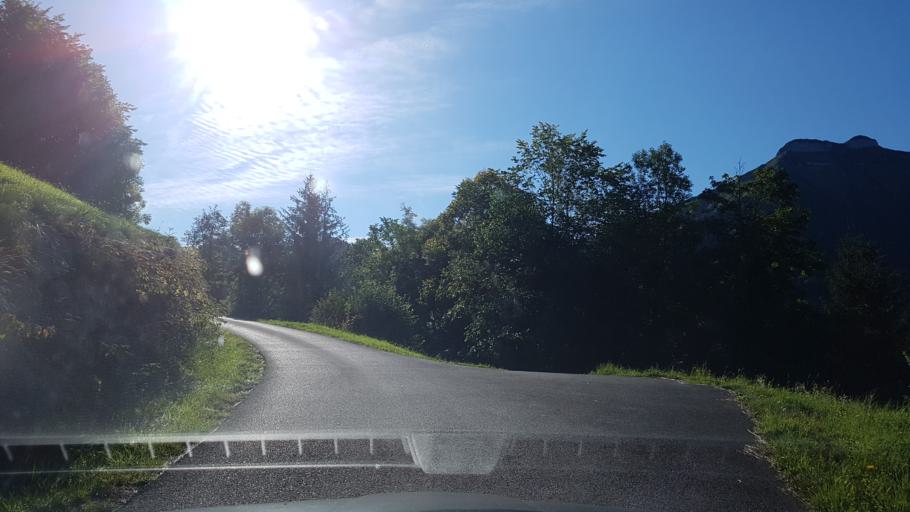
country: AT
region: Salzburg
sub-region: Politischer Bezirk Hallein
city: Krispl
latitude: 47.7026
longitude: 13.2264
